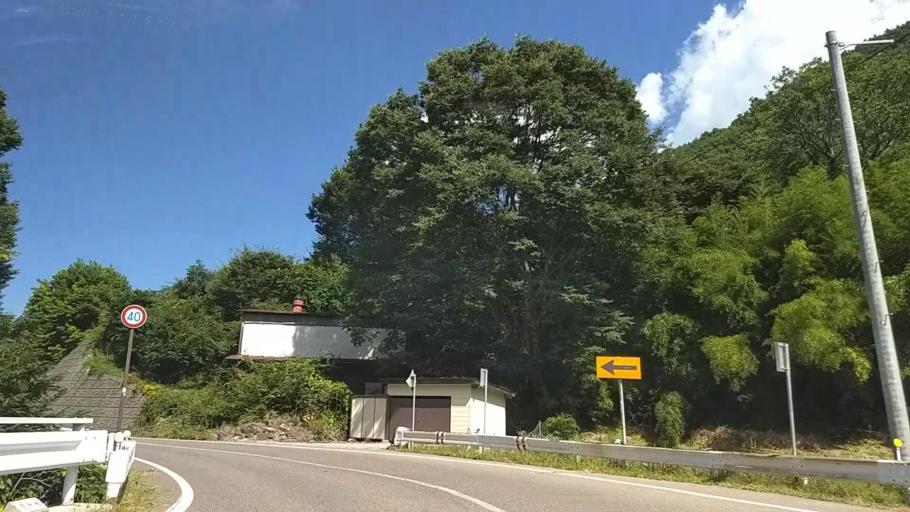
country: JP
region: Nagano
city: Matsumoto
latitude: 36.2123
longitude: 138.0544
